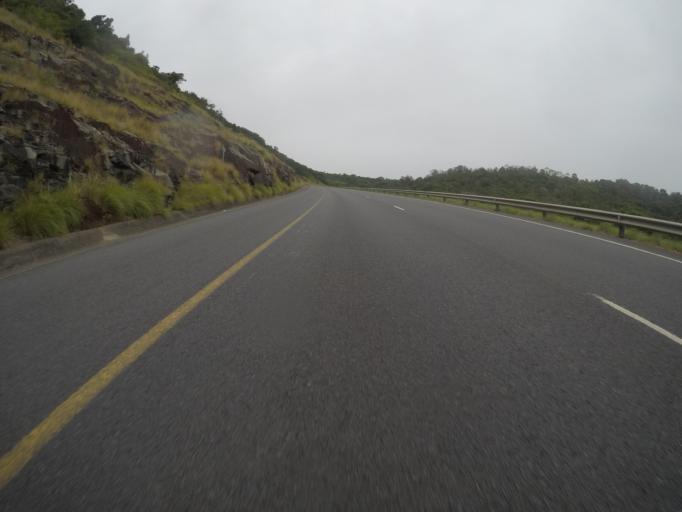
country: ZA
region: Eastern Cape
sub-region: Buffalo City Metropolitan Municipality
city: East London
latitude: -32.9711
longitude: 27.9066
